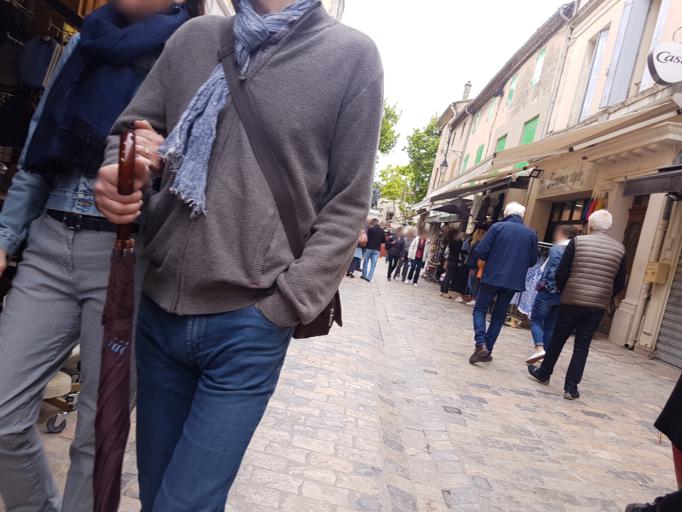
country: FR
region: Languedoc-Roussillon
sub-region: Departement du Gard
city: Aigues-Mortes
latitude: 43.5673
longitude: 4.1904
